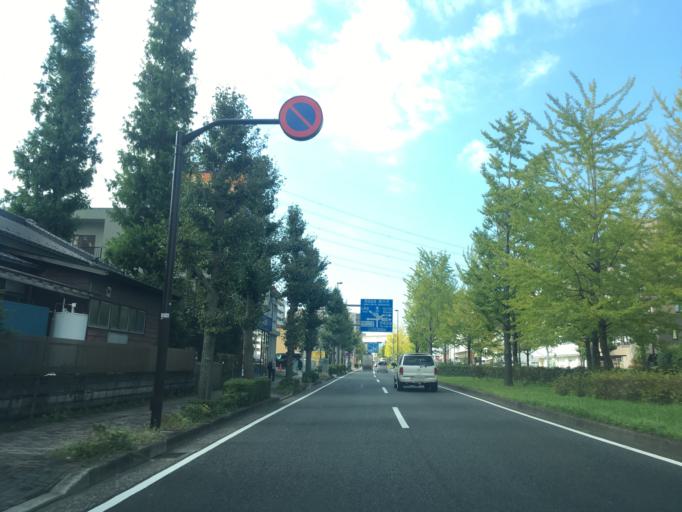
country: JP
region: Tokyo
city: Hino
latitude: 35.6280
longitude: 139.4284
